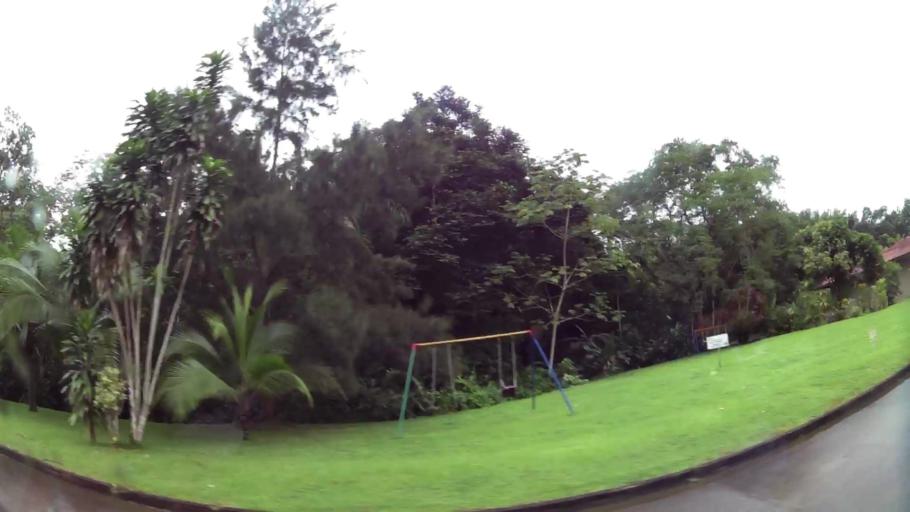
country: PA
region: Panama
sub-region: Distrito de Panama
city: Ancon
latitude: 8.9874
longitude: -79.5616
